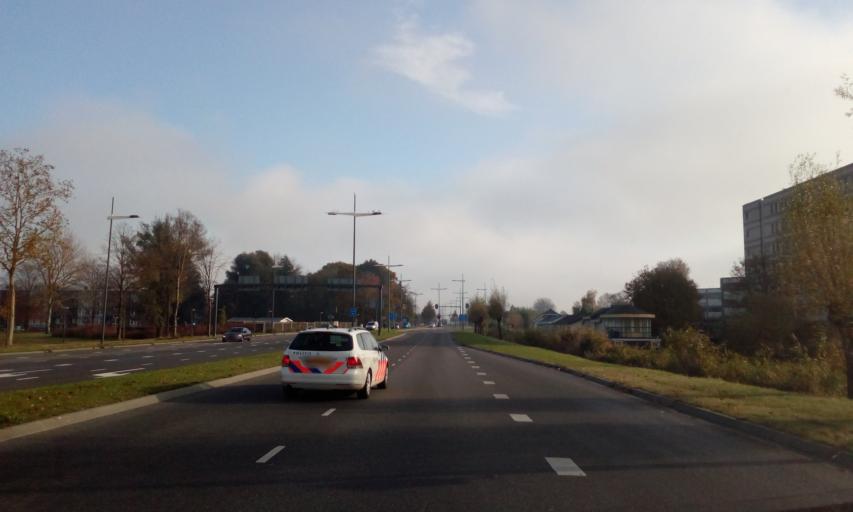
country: NL
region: Overijssel
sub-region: Gemeente Deventer
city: Deventer
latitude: 52.2533
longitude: 6.1810
